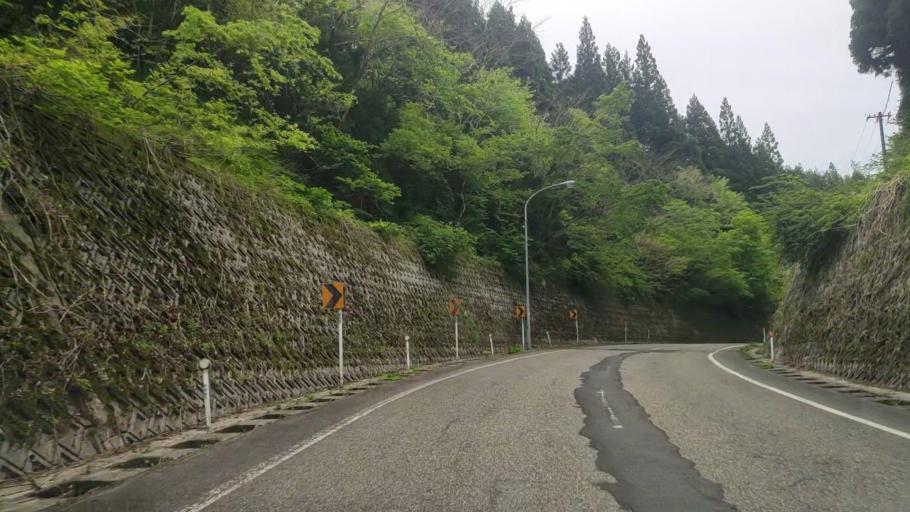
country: JP
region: Niigata
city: Gosen
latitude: 37.7137
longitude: 139.1119
